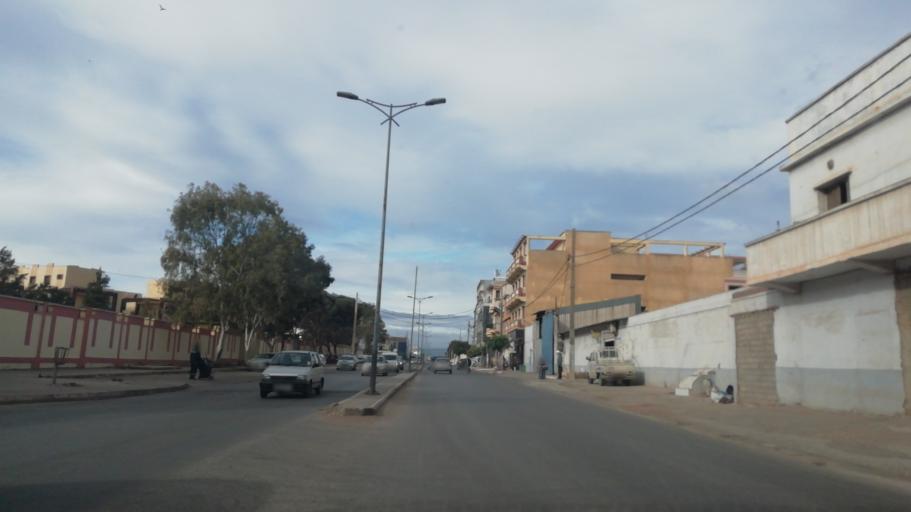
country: DZ
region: Oran
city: Bir el Djir
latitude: 35.7126
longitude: -0.5914
